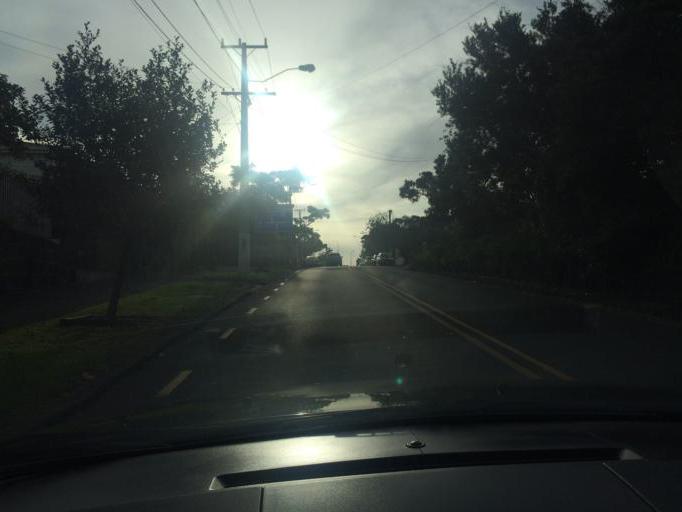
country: NZ
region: Auckland
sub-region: Auckland
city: Auckland
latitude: -36.8630
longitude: 174.7837
